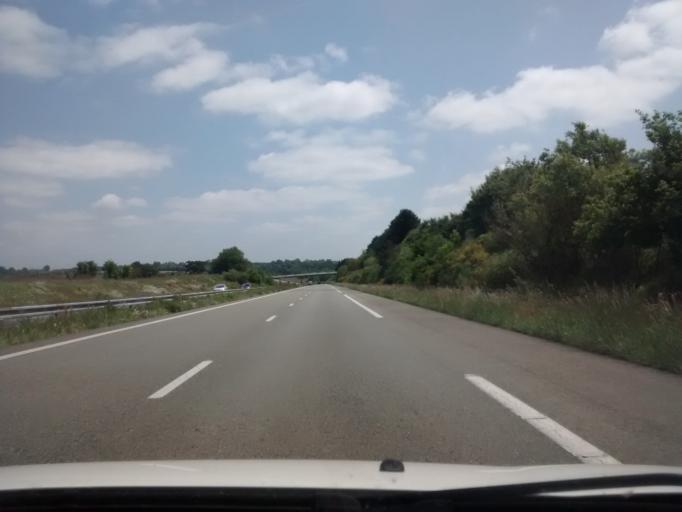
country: FR
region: Pays de la Loire
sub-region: Departement de la Mayenne
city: Argentre
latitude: 48.0790
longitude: -0.6545
